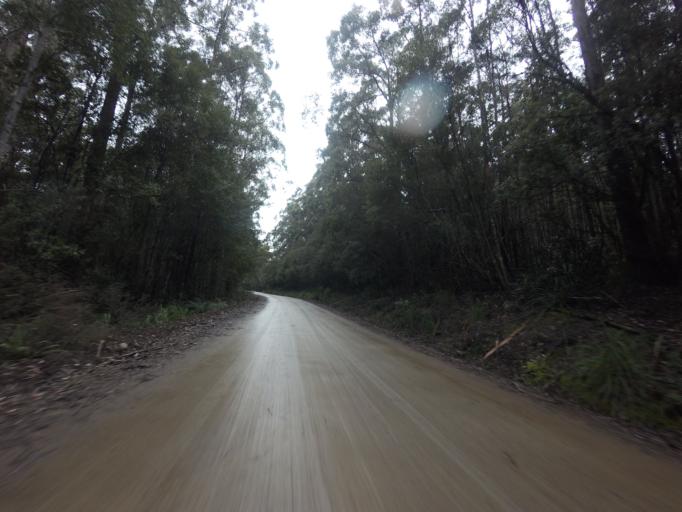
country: AU
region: Tasmania
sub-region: Huon Valley
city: Geeveston
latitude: -43.4945
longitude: 146.8806
